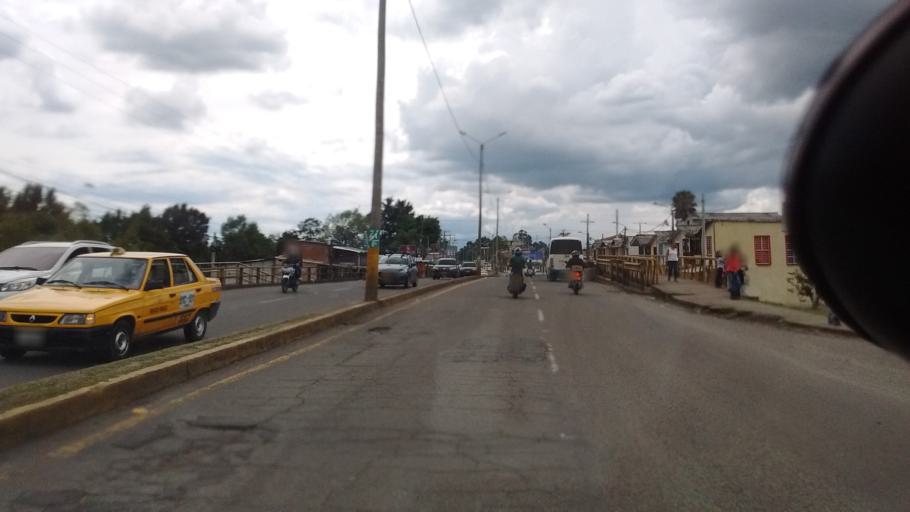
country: CO
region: Cauca
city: Popayan
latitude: 2.4813
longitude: -76.5694
